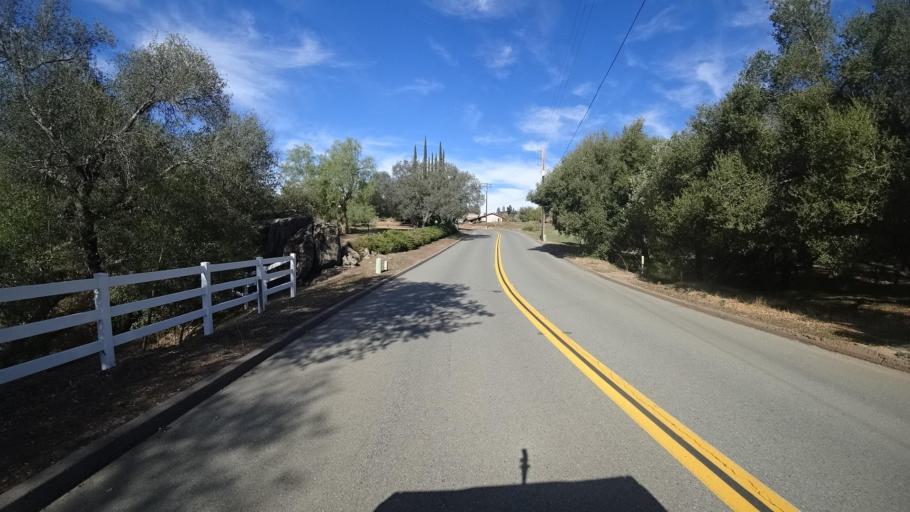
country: US
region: California
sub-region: San Diego County
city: Alpine
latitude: 32.8150
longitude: -116.7383
